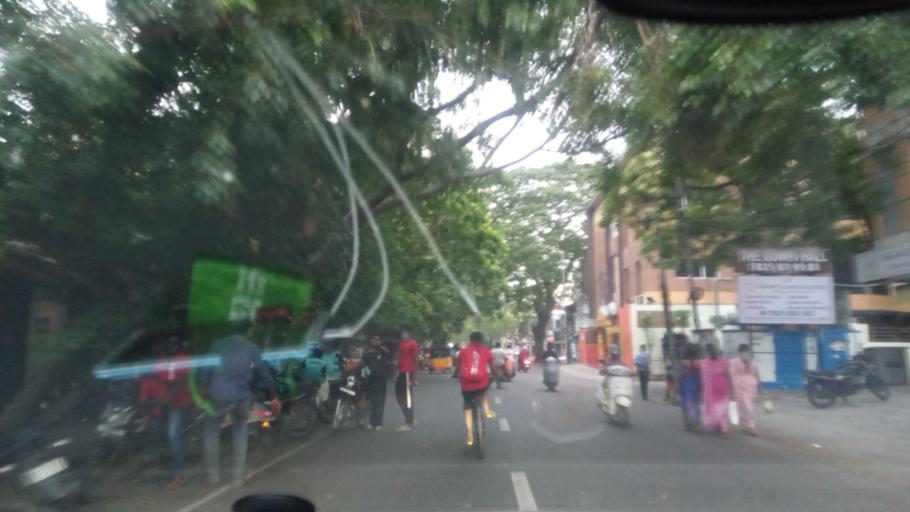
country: IN
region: Tamil Nadu
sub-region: Chennai
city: Chetput
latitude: 13.0421
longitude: 80.2219
